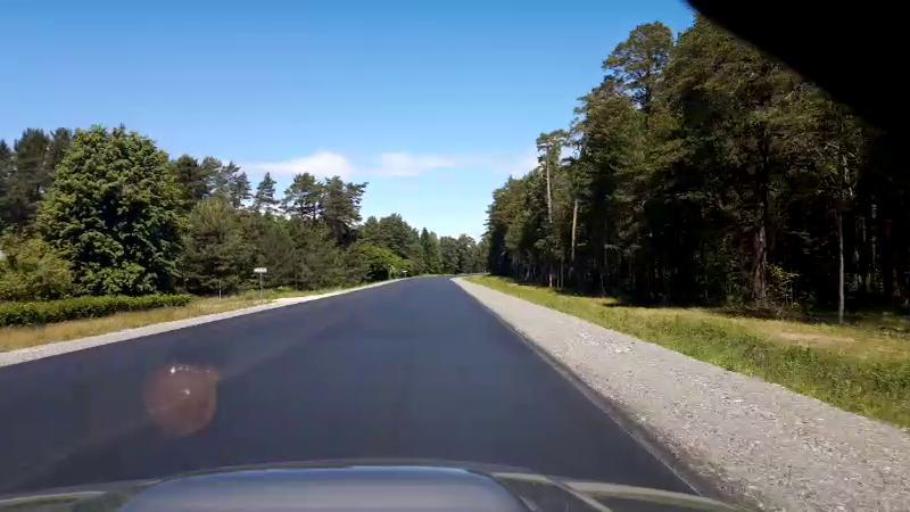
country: LV
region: Salacgrivas
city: Ainazi
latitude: 57.8314
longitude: 24.3446
